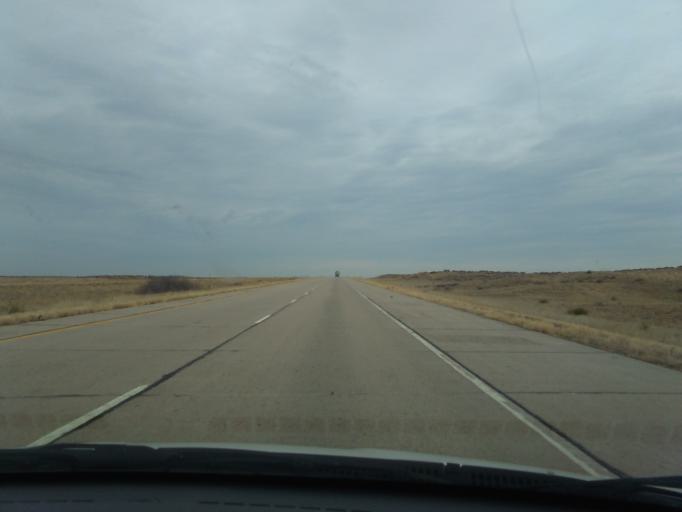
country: US
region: Colorado
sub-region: Weld County
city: Keenesburg
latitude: 40.1931
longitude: -104.2798
